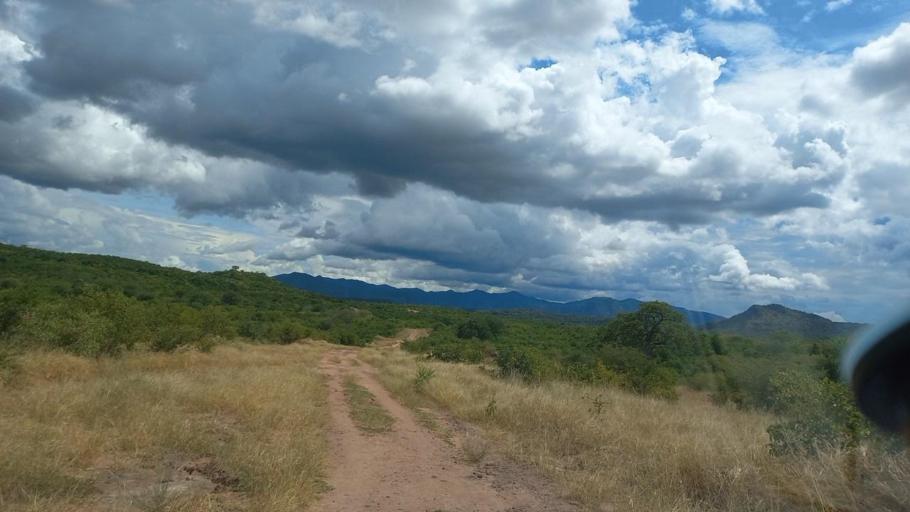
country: ZM
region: Lusaka
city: Luangwa
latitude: -15.6268
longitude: 30.3918
